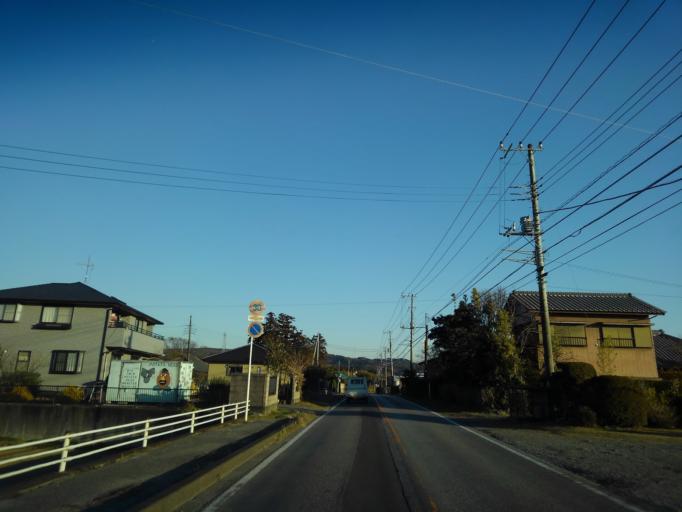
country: JP
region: Chiba
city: Kimitsu
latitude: 35.3028
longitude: 139.9715
